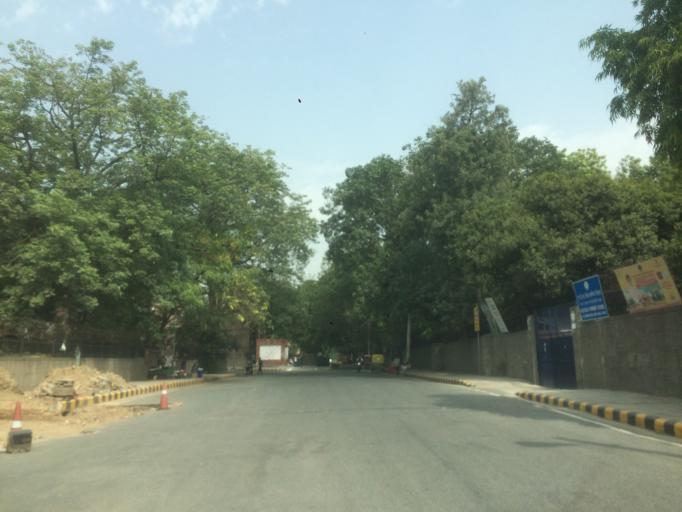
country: IN
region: NCT
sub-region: New Delhi
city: New Delhi
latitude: 28.6380
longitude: 77.2055
